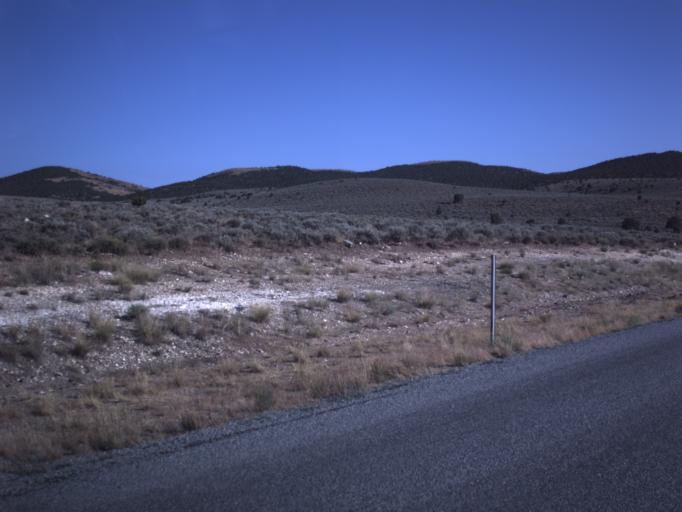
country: US
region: Utah
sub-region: Iron County
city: Parowan
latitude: 38.0296
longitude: -112.9983
